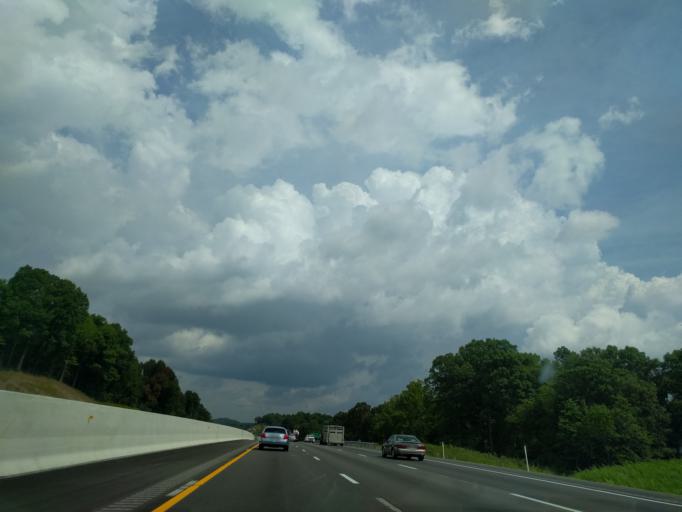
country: US
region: Kentucky
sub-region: Hart County
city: Munfordville
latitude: 37.3946
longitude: -85.8833
